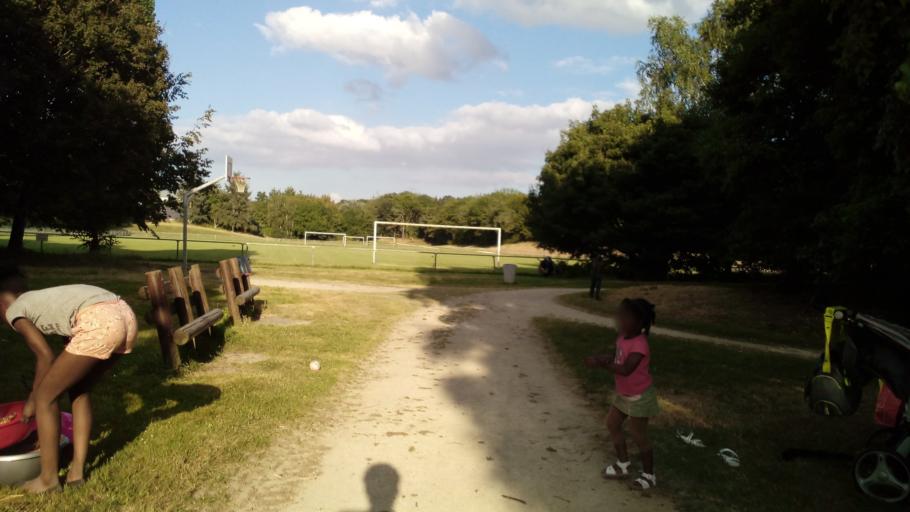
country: FR
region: Brittany
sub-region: Departement d'Ille-et-Vilaine
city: Rennes
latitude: 48.0824
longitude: -1.6585
